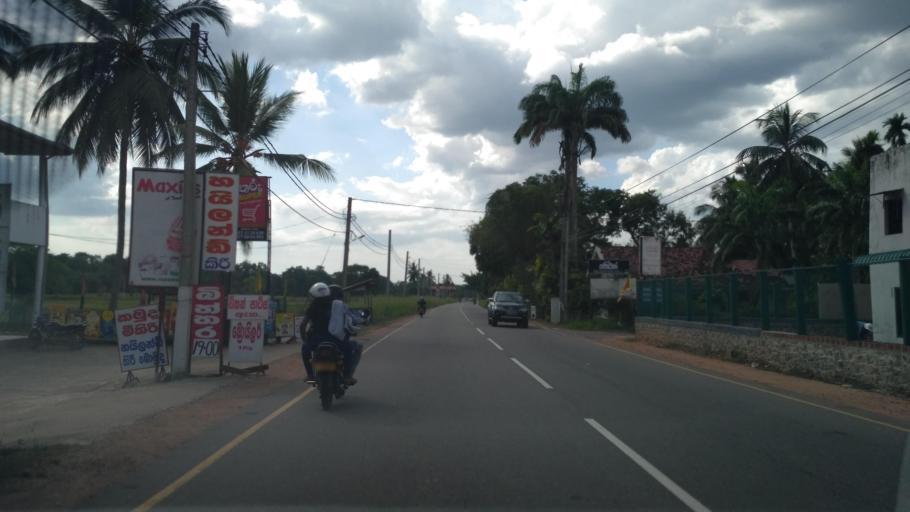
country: LK
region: North Western
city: Kuliyapitiya
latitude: 7.3255
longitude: 80.0359
